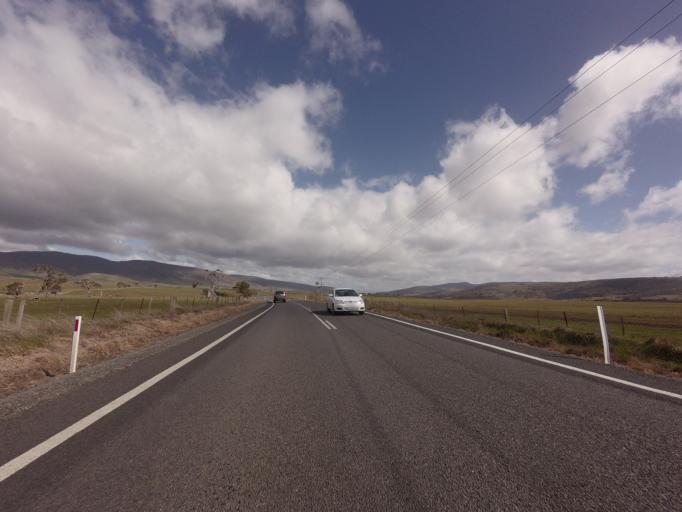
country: AU
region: Tasmania
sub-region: Northern Midlands
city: Evandale
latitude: -41.8025
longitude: 147.6870
